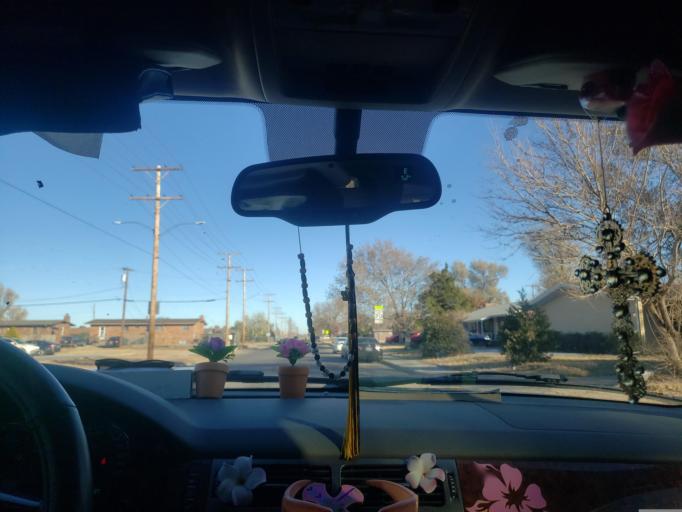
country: US
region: Kansas
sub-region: Finney County
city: Garden City
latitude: 37.9666
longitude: -100.8553
